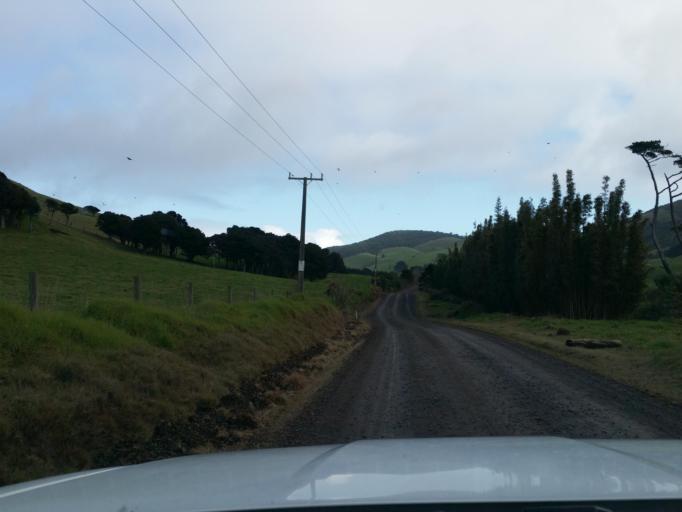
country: NZ
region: Northland
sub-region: Kaipara District
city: Dargaville
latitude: -35.7496
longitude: 173.5869
